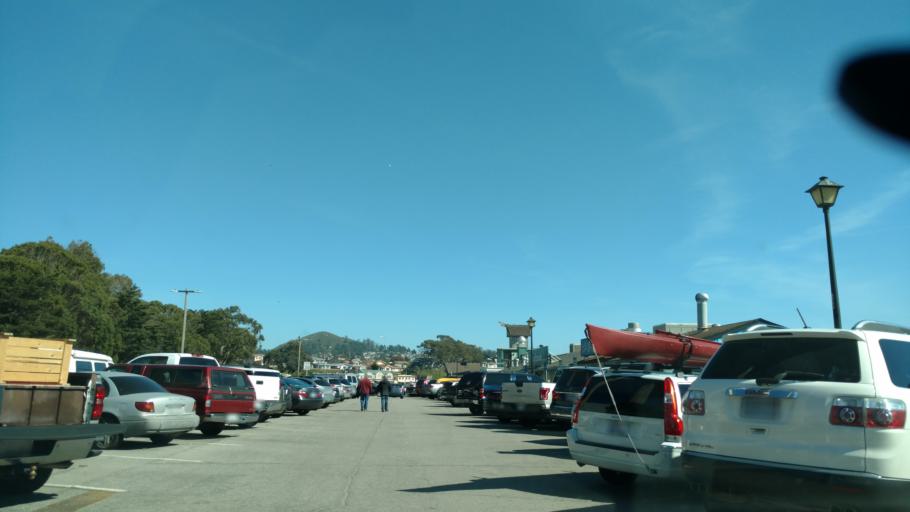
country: US
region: California
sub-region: San Luis Obispo County
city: Morro Bay
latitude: 35.3713
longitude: -120.8578
